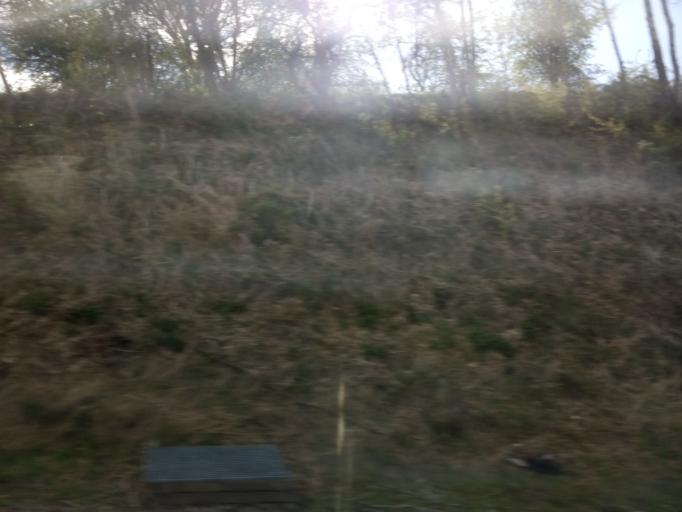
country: GB
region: England
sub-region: County Durham
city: Chester-le-Street
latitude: 54.8218
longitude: -1.5796
